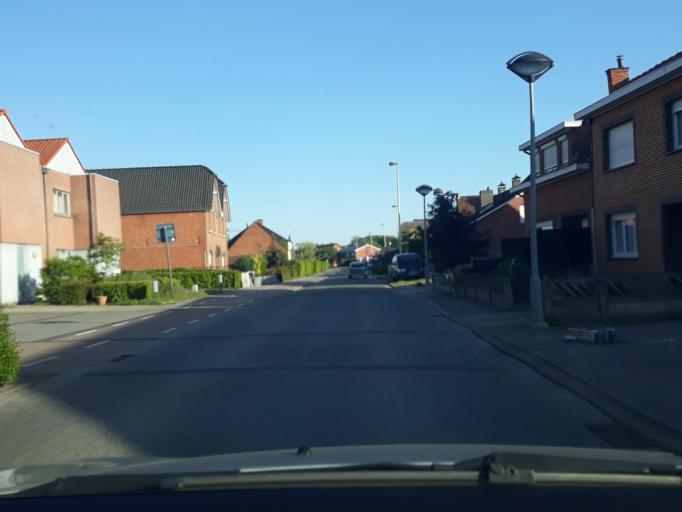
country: BE
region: Flanders
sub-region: Provincie Antwerpen
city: Grobbendonk
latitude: 51.1977
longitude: 4.7326
